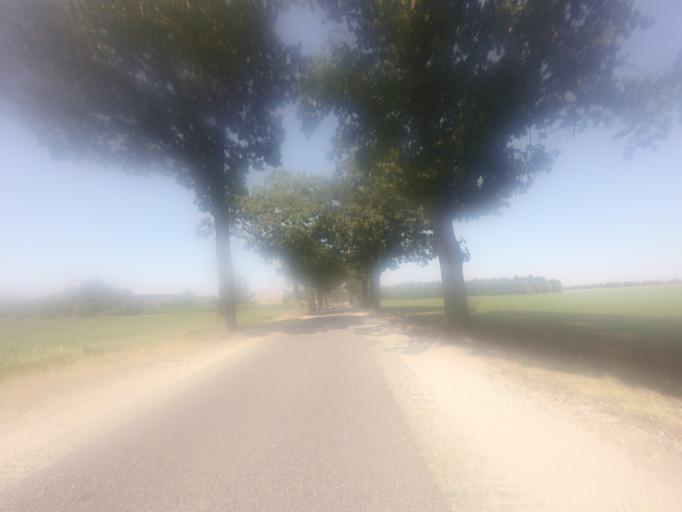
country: NL
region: North Brabant
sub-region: Gemeente Oirschot
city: Oostelbeers
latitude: 51.4814
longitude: 5.2693
